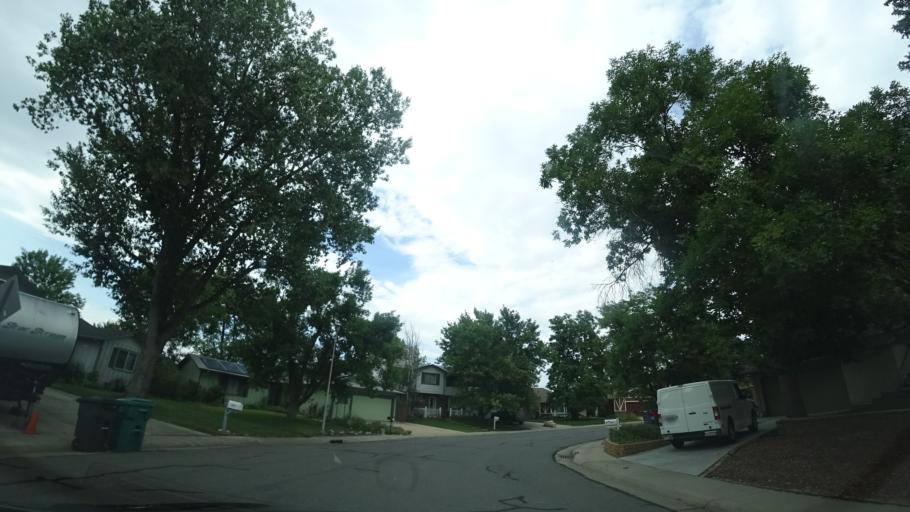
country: US
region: Colorado
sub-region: Jefferson County
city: Lakewood
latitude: 39.7063
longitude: -105.0995
